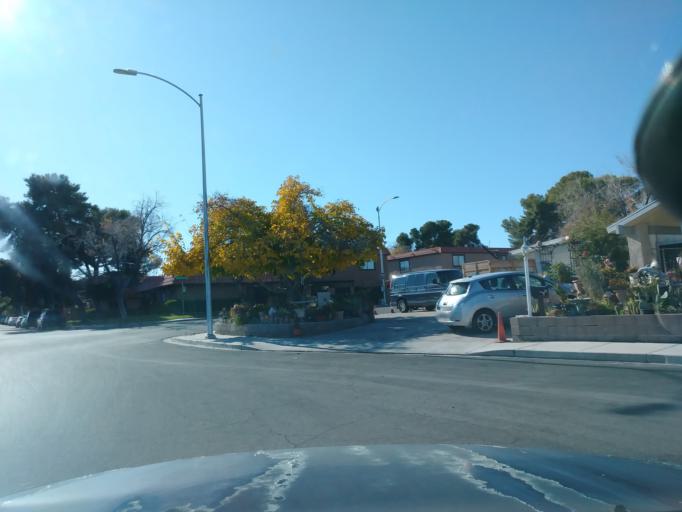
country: US
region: Nevada
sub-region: Clark County
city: Spring Valley
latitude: 36.1778
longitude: -115.2378
